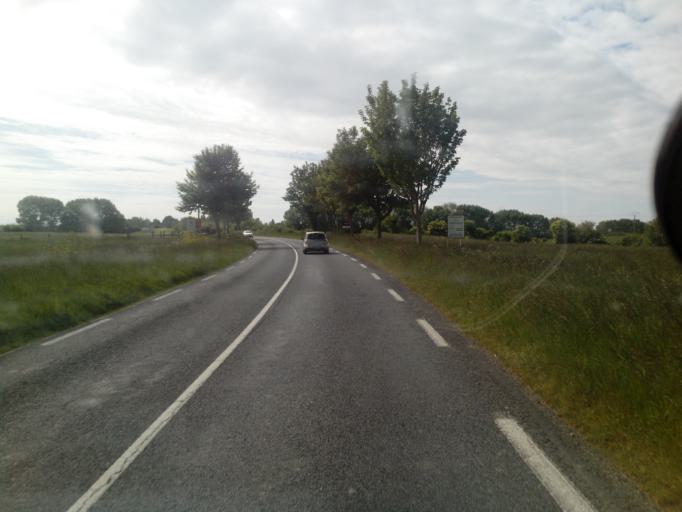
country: FR
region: Lower Normandy
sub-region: Departement du Calvados
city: Dives-sur-Mer
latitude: 49.2740
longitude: -0.1067
